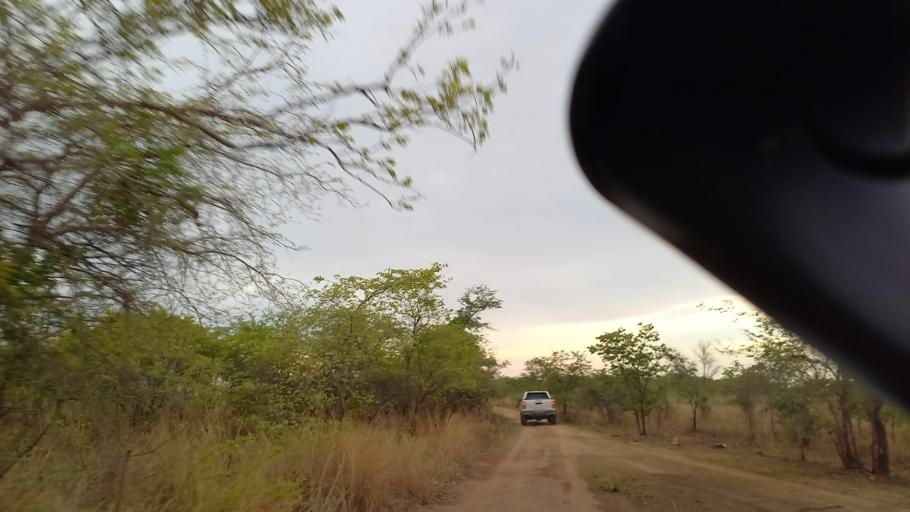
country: ZM
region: Lusaka
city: Kafue
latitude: -16.0483
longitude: 28.3251
